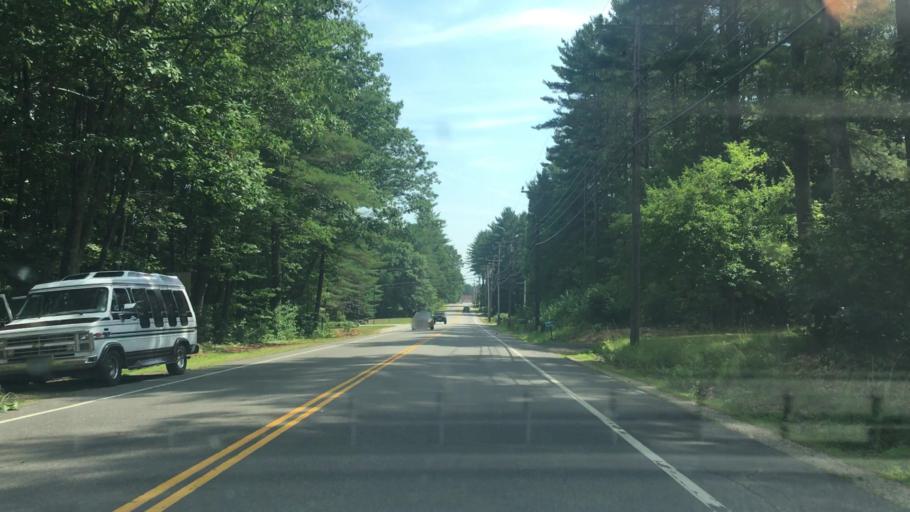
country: US
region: New Hampshire
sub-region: Strafford County
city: Rochester
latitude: 43.3633
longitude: -70.9803
